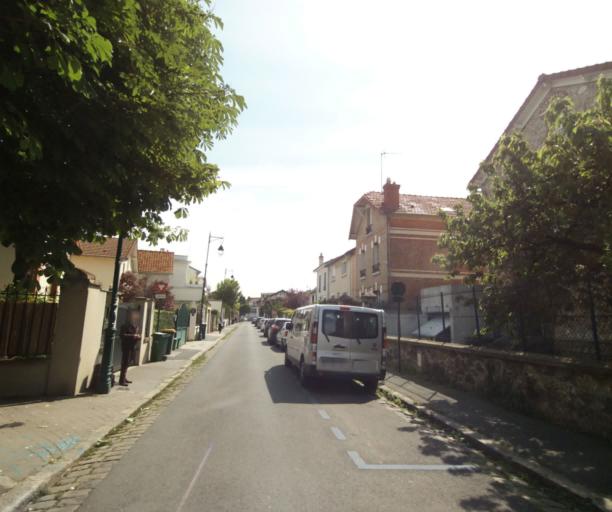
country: FR
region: Ile-de-France
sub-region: Departement des Hauts-de-Seine
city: La Garenne-Colombes
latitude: 48.9133
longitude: 2.2425
